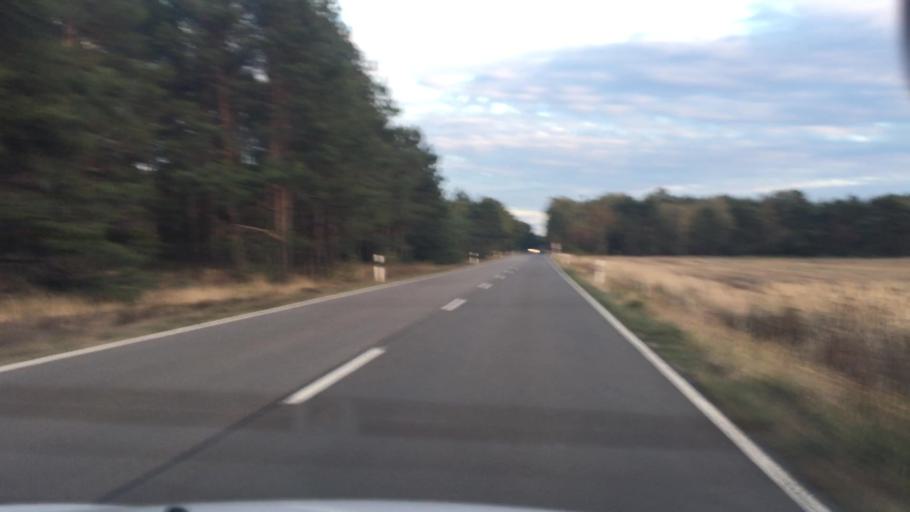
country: DE
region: Brandenburg
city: Welzow
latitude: 51.5707
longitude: 14.0995
